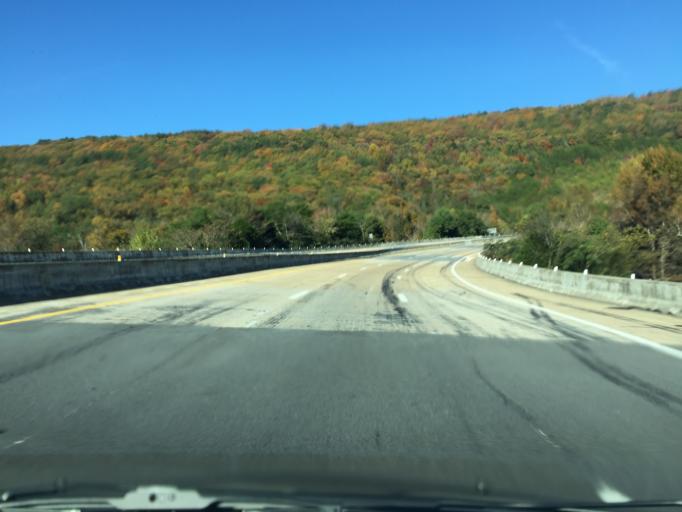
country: US
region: Tennessee
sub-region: Hamilton County
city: Soddy-Daisy
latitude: 35.3043
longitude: -85.1623
